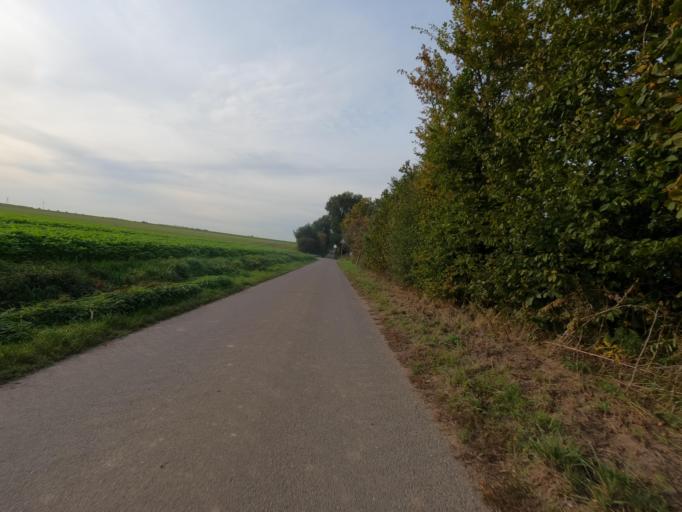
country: DE
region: North Rhine-Westphalia
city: Huckelhoven
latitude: 51.0325
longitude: 6.1685
